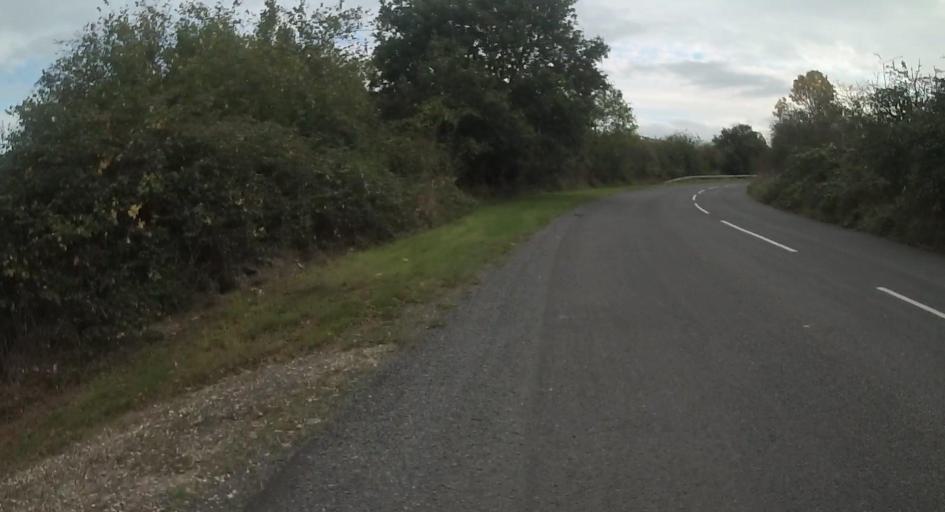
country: GB
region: England
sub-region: Hampshire
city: Odiham
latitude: 51.2912
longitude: -0.8935
